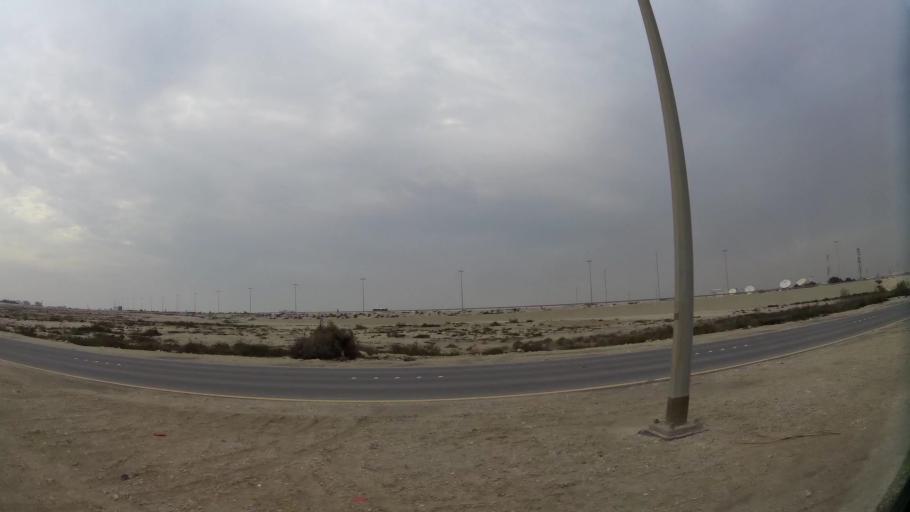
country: BH
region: Northern
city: Sitrah
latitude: 26.0687
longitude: 50.6162
